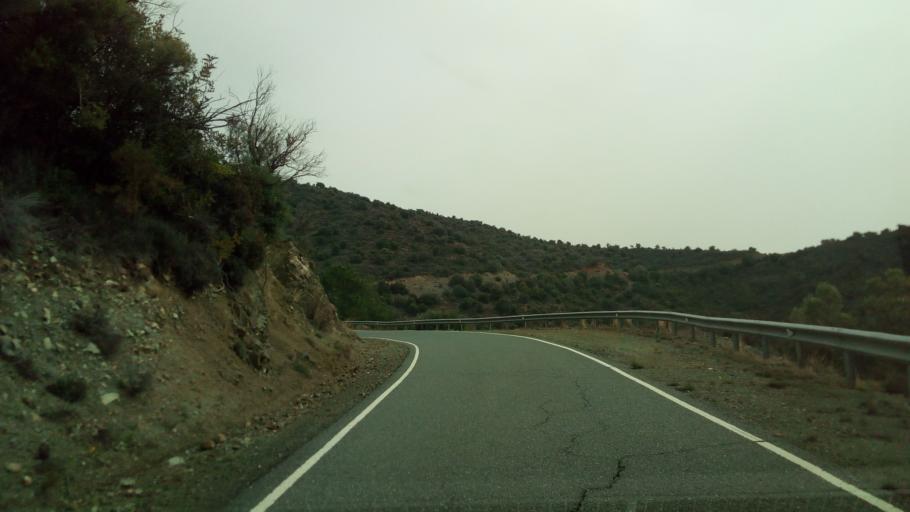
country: CY
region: Limassol
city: Mouttagiaka
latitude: 34.8060
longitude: 33.0853
